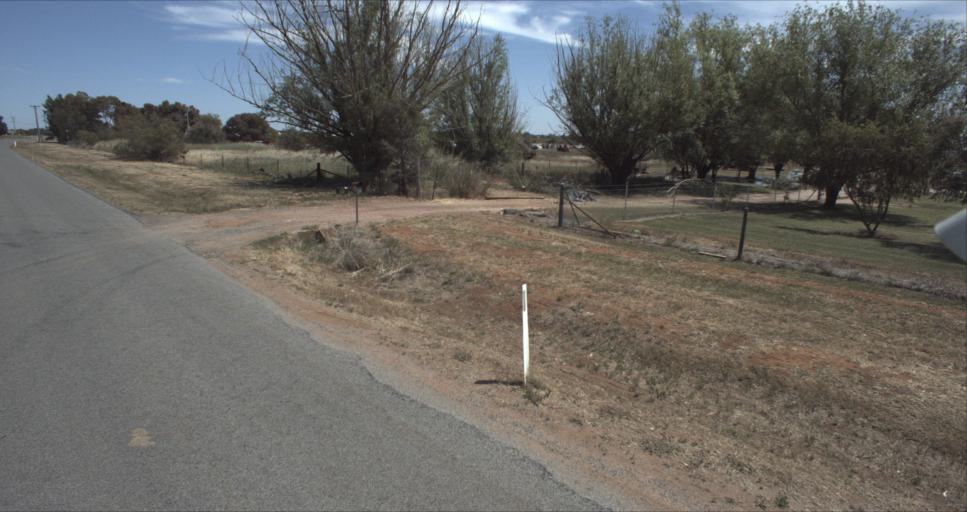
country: AU
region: New South Wales
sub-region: Leeton
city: Leeton
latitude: -34.5674
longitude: 146.4480
